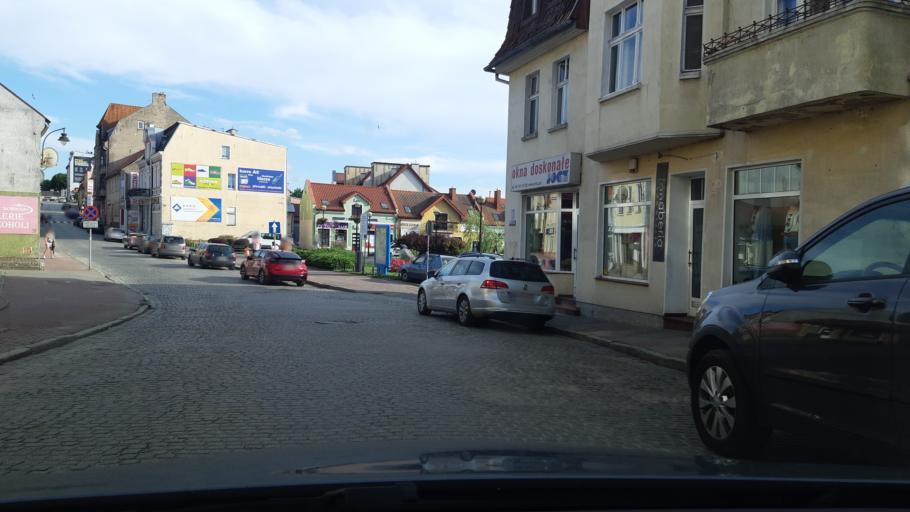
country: PL
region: Warmian-Masurian Voivodeship
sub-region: Powiat mragowski
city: Mragowo
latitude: 53.8696
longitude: 21.3043
